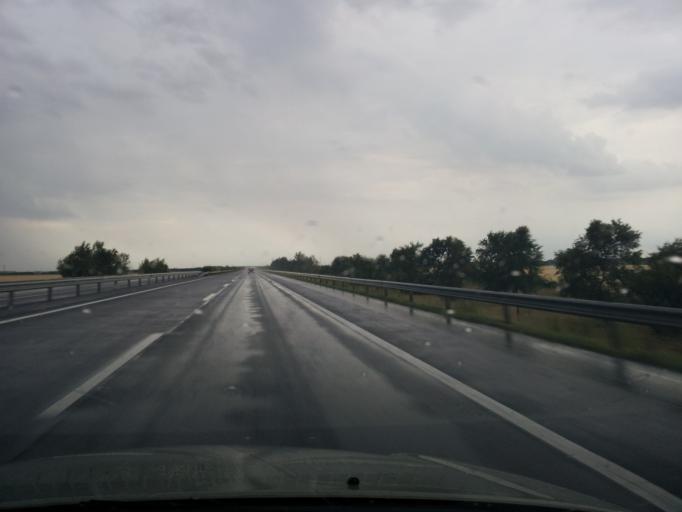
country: HU
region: Borsod-Abauj-Zemplen
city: Onod
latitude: 48.0112
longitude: 20.8784
